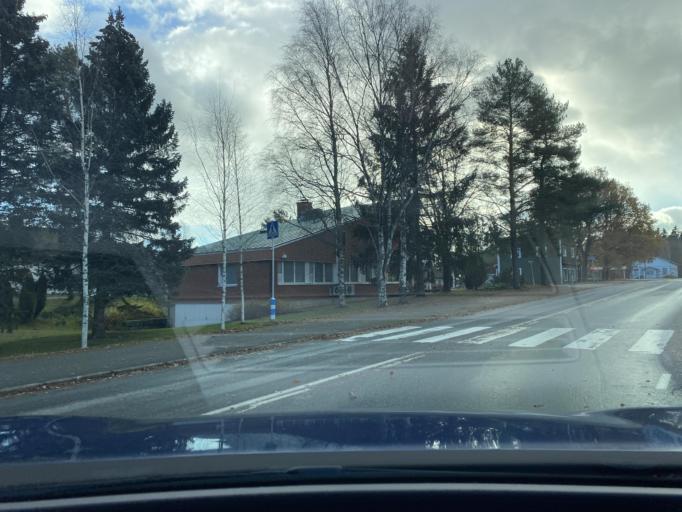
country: FI
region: Varsinais-Suomi
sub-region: Loimaa
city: Aura
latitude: 60.7197
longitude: 22.6035
